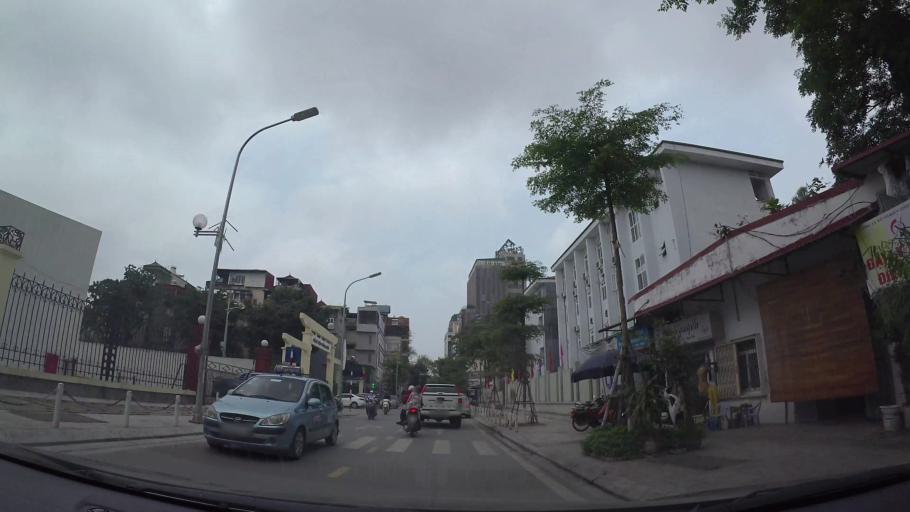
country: VN
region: Ha Noi
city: Hai BaTrung
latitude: 21.0127
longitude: 105.8464
